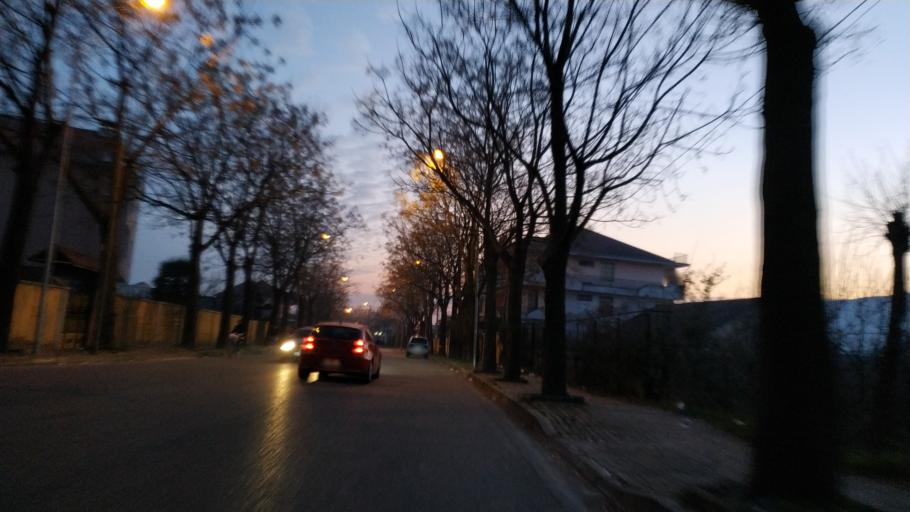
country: AL
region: Shkoder
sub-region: Rrethi i Shkodres
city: Shkoder
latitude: 42.0753
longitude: 19.5029
